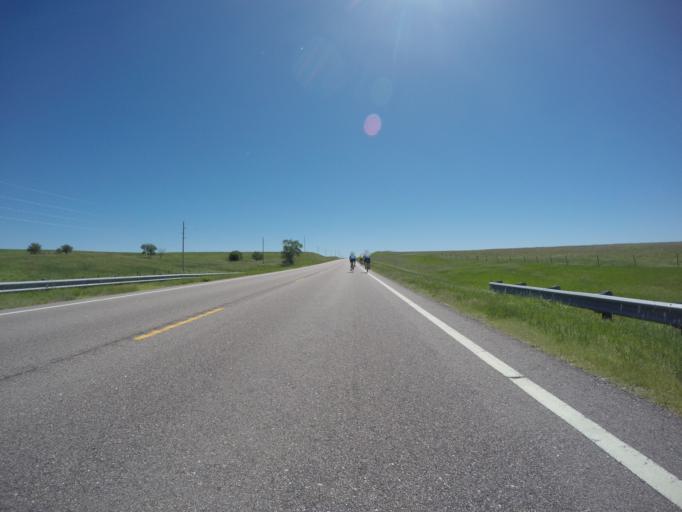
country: US
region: Kansas
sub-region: Norton County
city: Norton
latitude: 39.8283
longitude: -99.6962
